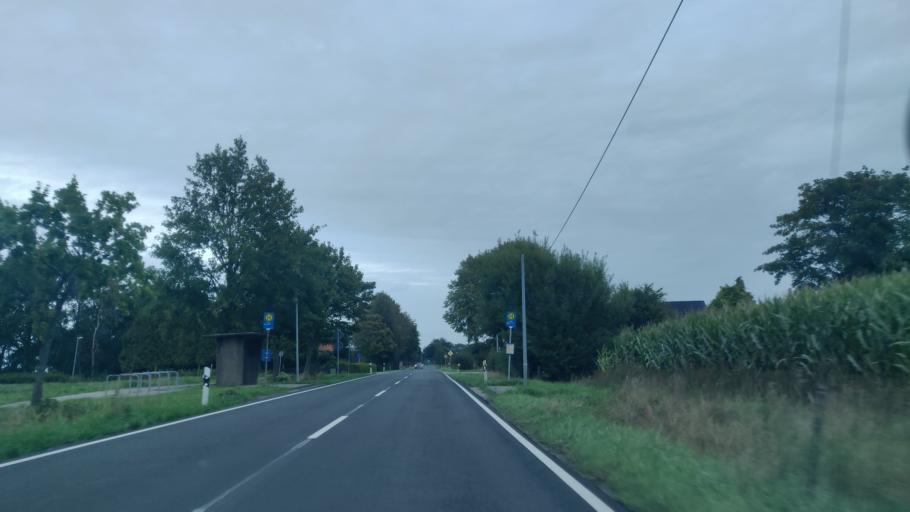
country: DE
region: Lower Saxony
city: Aurich
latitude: 53.4852
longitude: 7.4246
